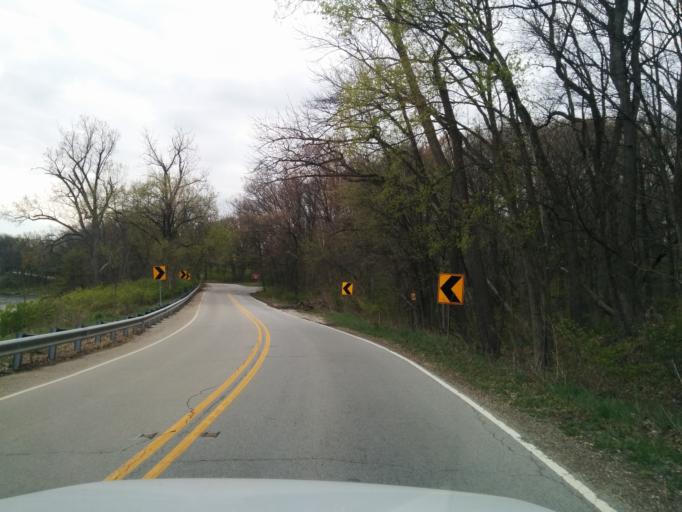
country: US
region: Illinois
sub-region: DuPage County
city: Burr Ridge
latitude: 41.7160
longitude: -87.8935
